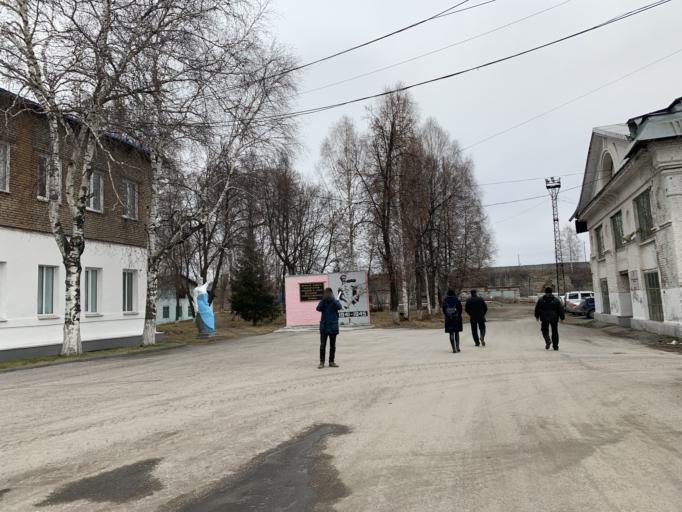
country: RU
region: Chelyabinsk
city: Nyazepetrovsk
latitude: 56.0537
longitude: 59.5899
